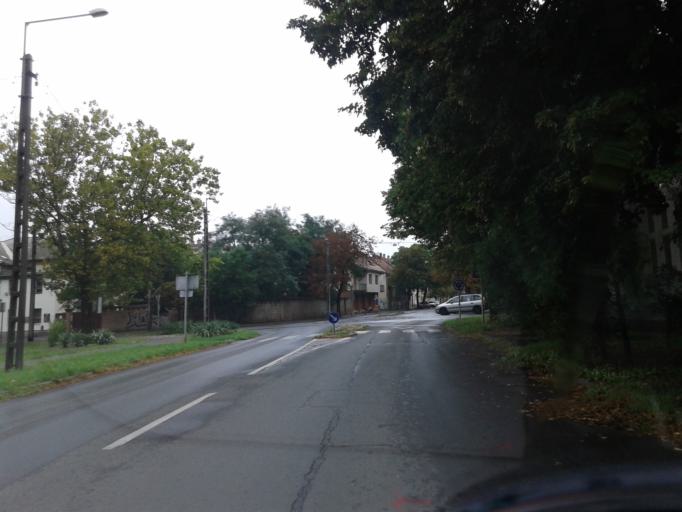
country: HU
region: Csongrad
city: Szeged
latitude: 46.2414
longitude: 20.1377
